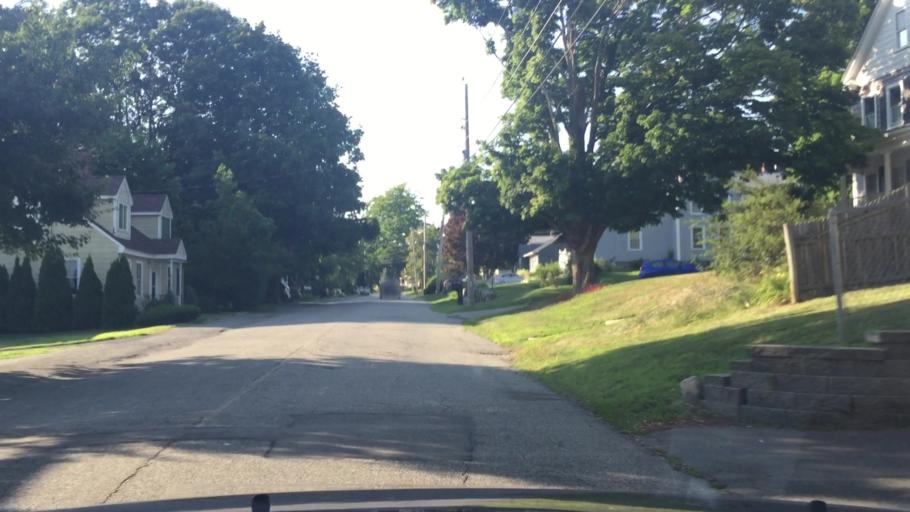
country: US
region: Massachusetts
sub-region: Essex County
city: North Andover
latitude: 42.7047
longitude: -71.1249
